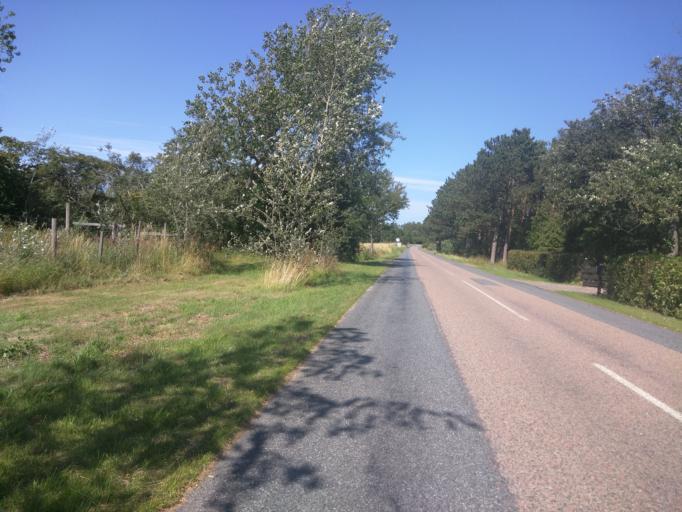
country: DK
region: Zealand
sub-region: Kalundborg Kommune
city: Svebolle
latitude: 55.6923
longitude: 11.2489
